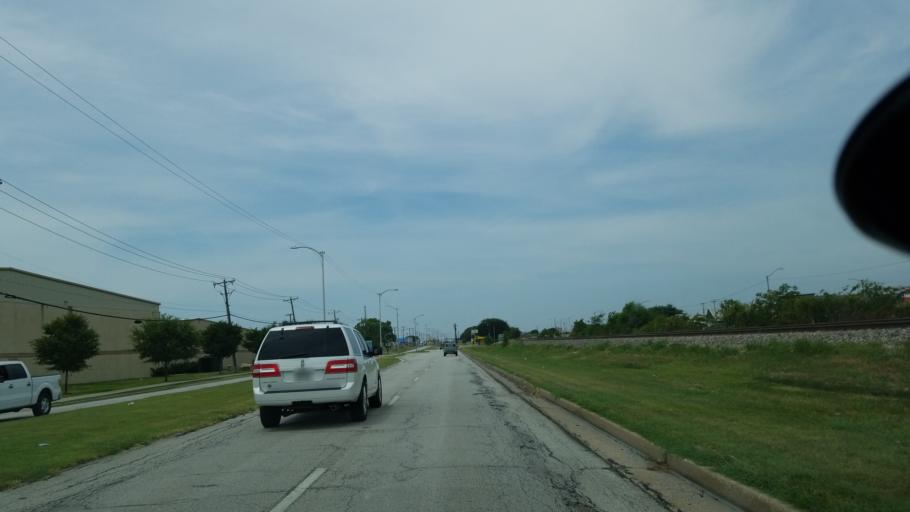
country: US
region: Texas
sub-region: Dallas County
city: Grand Prairie
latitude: 32.7390
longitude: -97.0379
